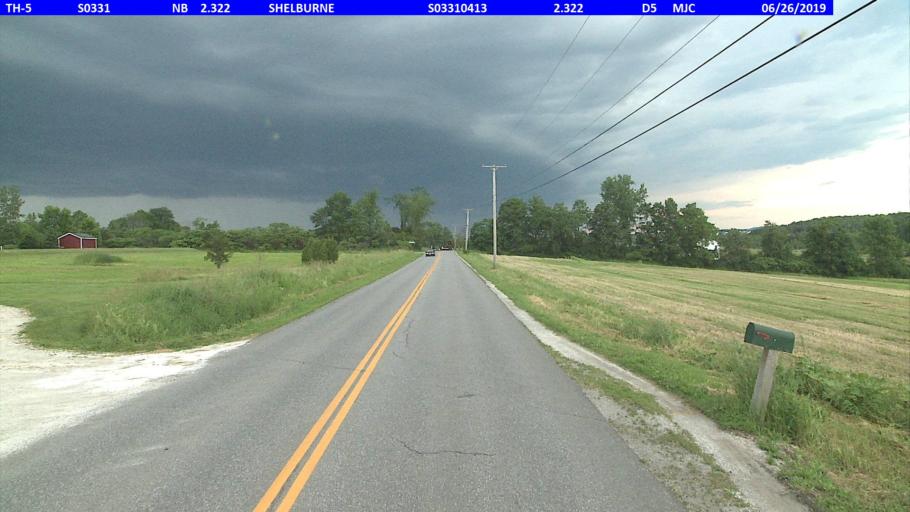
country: US
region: Vermont
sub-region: Chittenden County
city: South Burlington
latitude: 44.4039
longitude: -73.1783
